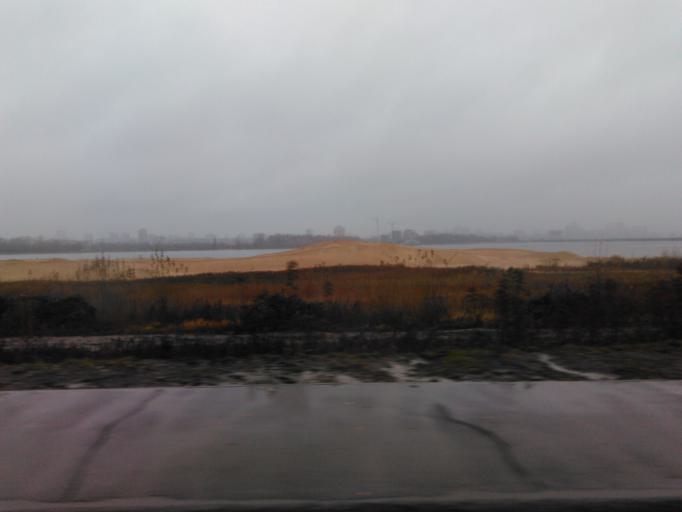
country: RU
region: Tatarstan
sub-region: Gorod Kazan'
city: Kazan
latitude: 55.7969
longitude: 49.0861
